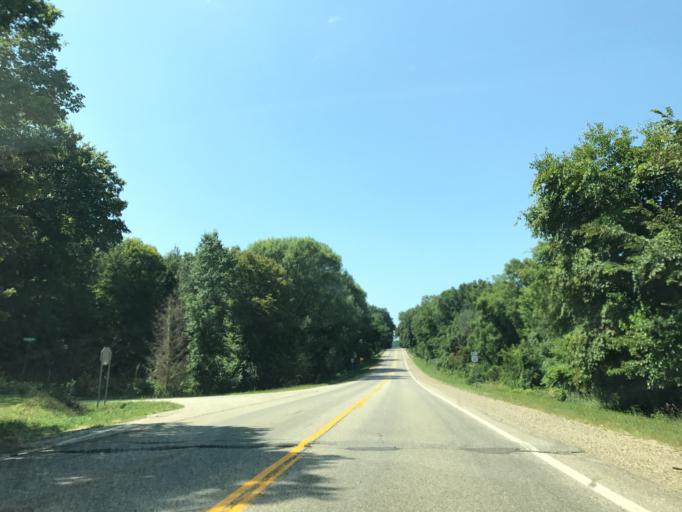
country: US
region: Michigan
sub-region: Berrien County
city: Buchanan
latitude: 41.8051
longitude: -86.3770
